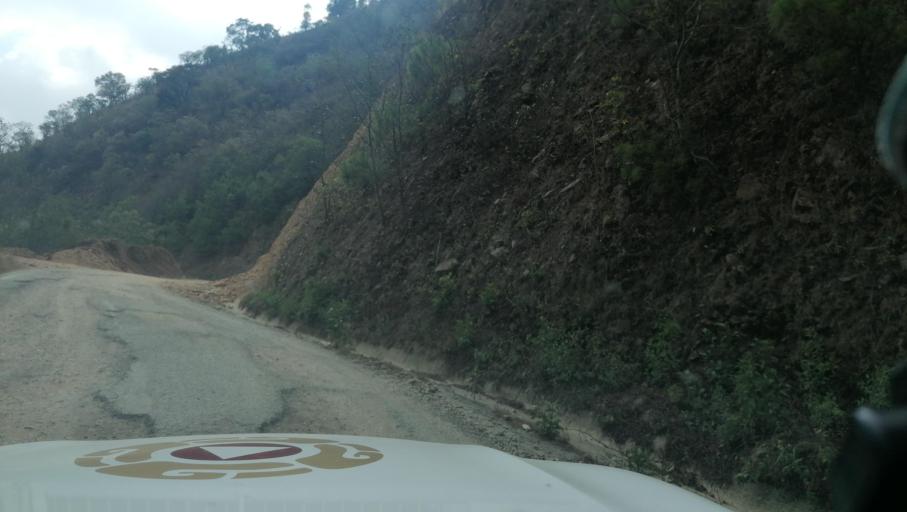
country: GT
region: San Marcos
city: Tacana
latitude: 15.2284
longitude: -92.1936
